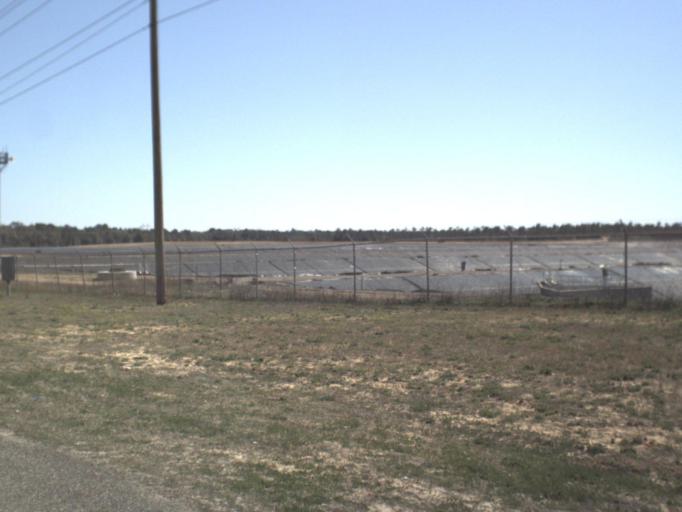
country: US
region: Florida
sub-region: Leon County
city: Tallahassee
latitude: 30.3918
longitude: -84.3191
